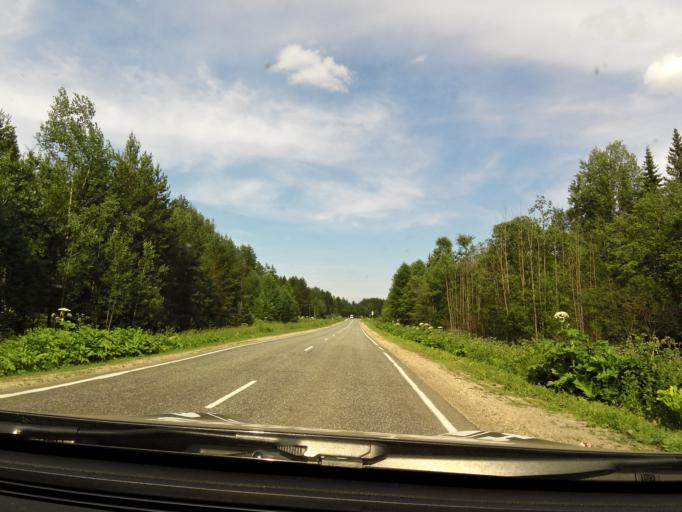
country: RU
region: Kirov
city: Slobodskoy
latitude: 58.7725
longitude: 50.3764
